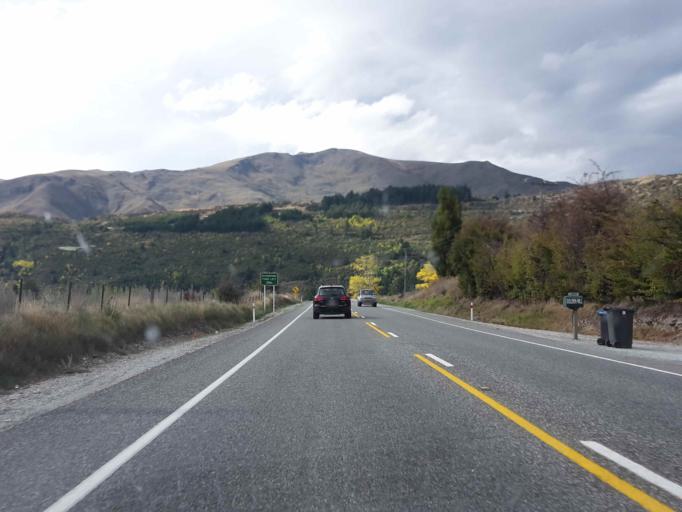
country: NZ
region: Otago
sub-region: Queenstown-Lakes District
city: Arrowtown
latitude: -44.9796
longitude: 168.8446
